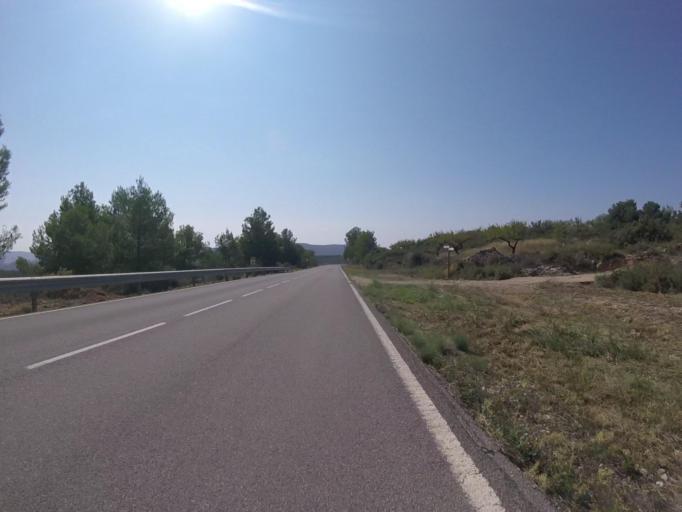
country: ES
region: Valencia
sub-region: Provincia de Castello
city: Adzaneta
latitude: 40.2408
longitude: -0.1887
